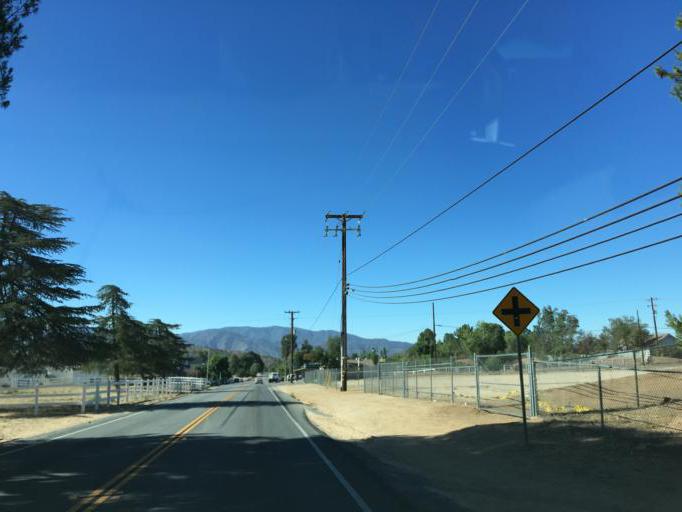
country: US
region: California
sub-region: Los Angeles County
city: Agua Dulce
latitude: 34.4974
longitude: -118.3262
